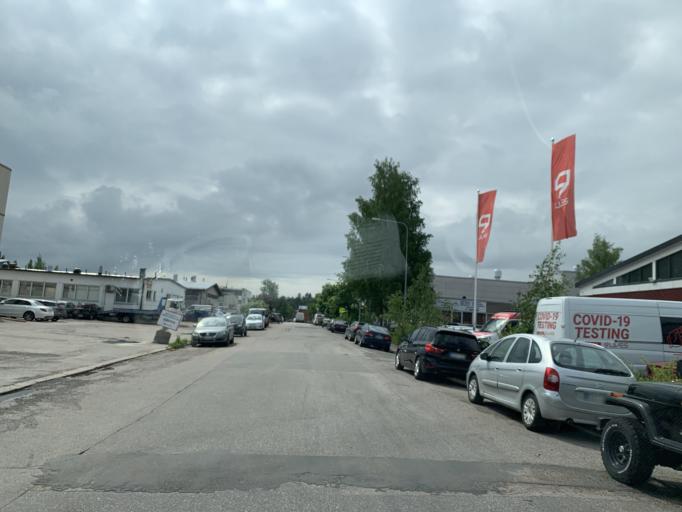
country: FI
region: Uusimaa
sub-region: Helsinki
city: Vantaa
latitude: 60.2549
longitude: 25.0267
